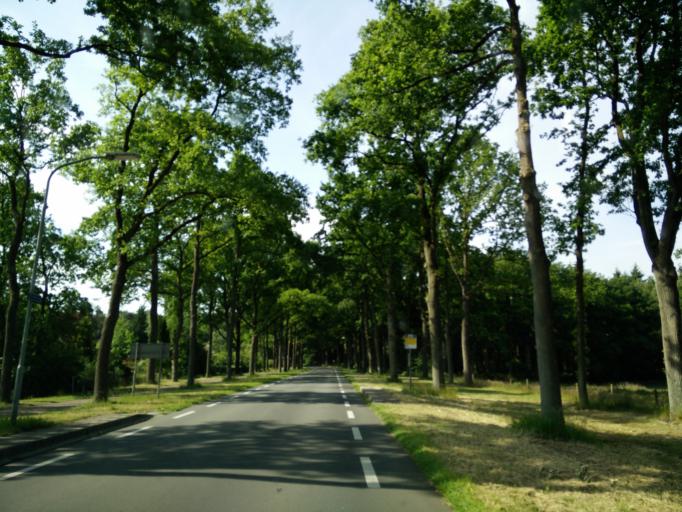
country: NL
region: Drenthe
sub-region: Gemeente Borger-Odoorn
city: Borger
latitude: 52.9646
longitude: 6.7888
